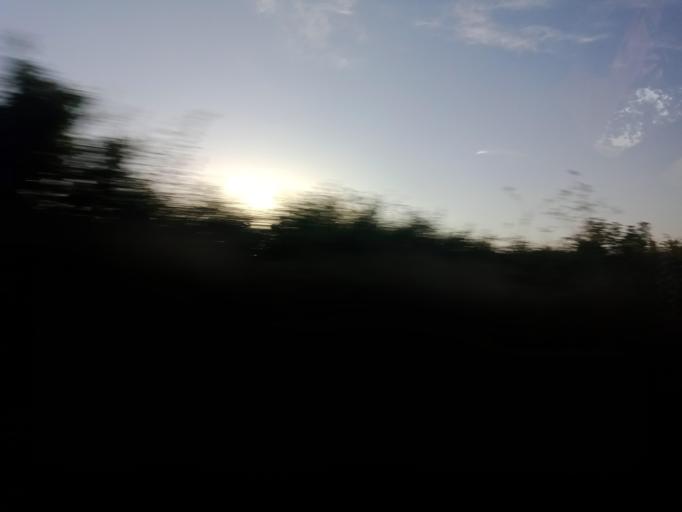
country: IE
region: Leinster
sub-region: Kilkenny
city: Castlecomer
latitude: 52.7398
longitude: -7.2370
